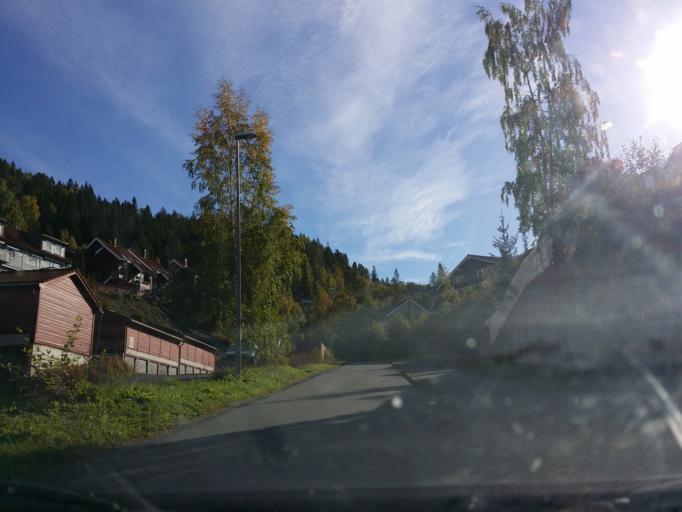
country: NO
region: Akershus
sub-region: Baerum
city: Sandvika
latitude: 59.9418
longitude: 10.5185
